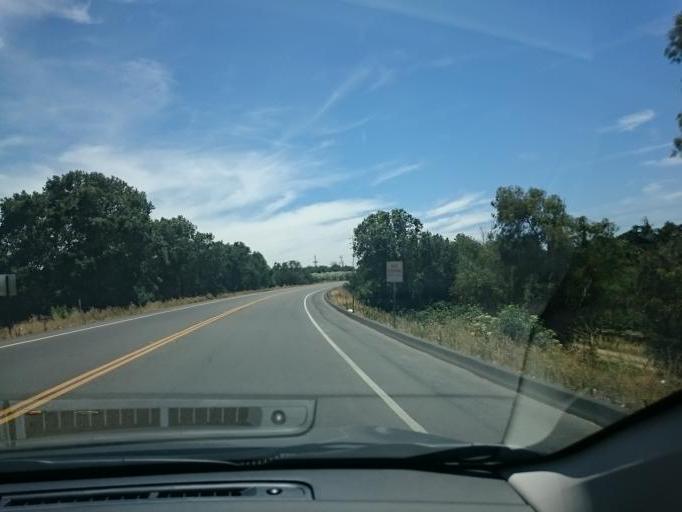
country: US
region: California
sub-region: Stanislaus County
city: Hughson
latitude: 37.6156
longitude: -120.8453
